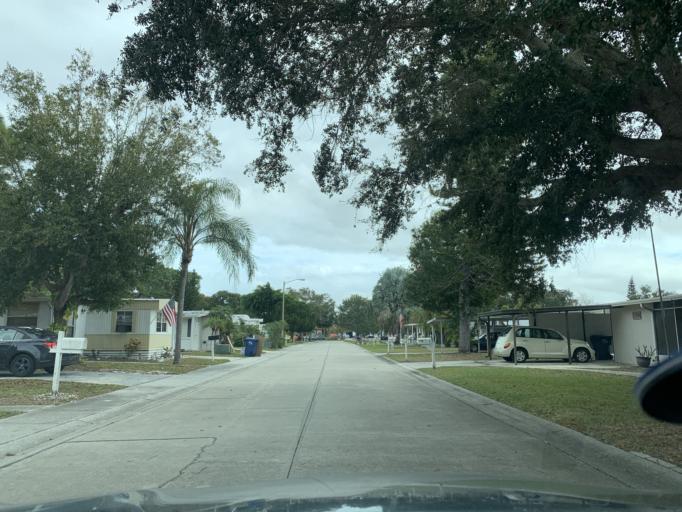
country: US
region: Florida
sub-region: Pinellas County
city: Ridgecrest
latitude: 27.8842
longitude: -82.7899
